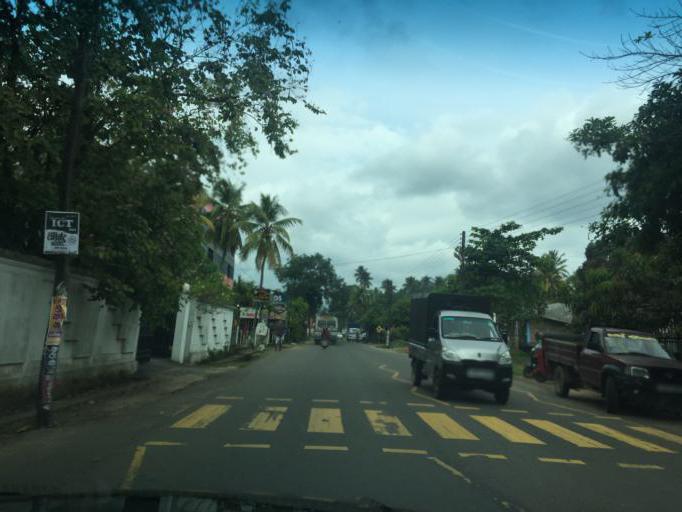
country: LK
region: Western
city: Horana South
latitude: 6.7072
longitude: 80.0682
